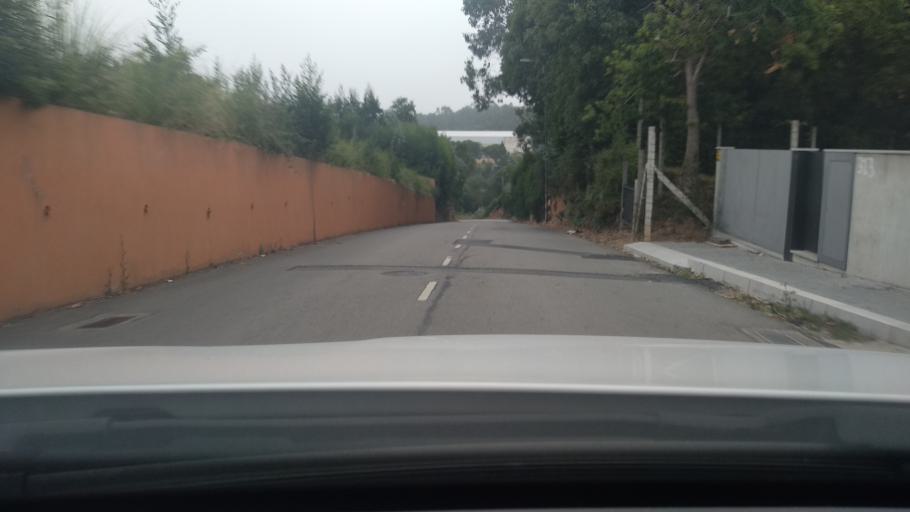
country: PT
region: Aveiro
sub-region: Espinho
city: Silvalde
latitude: 40.9952
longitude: -8.6266
